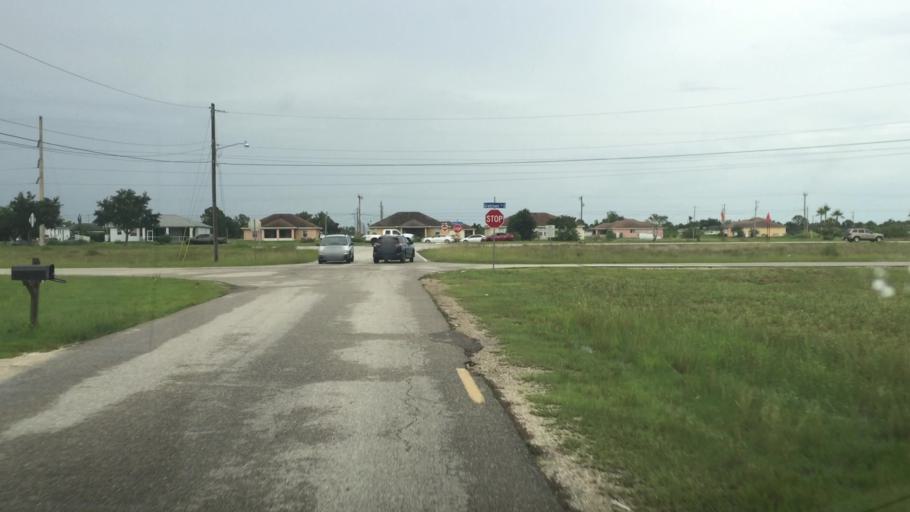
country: US
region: Florida
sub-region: Lee County
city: Gateway
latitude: 26.5885
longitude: -81.7134
